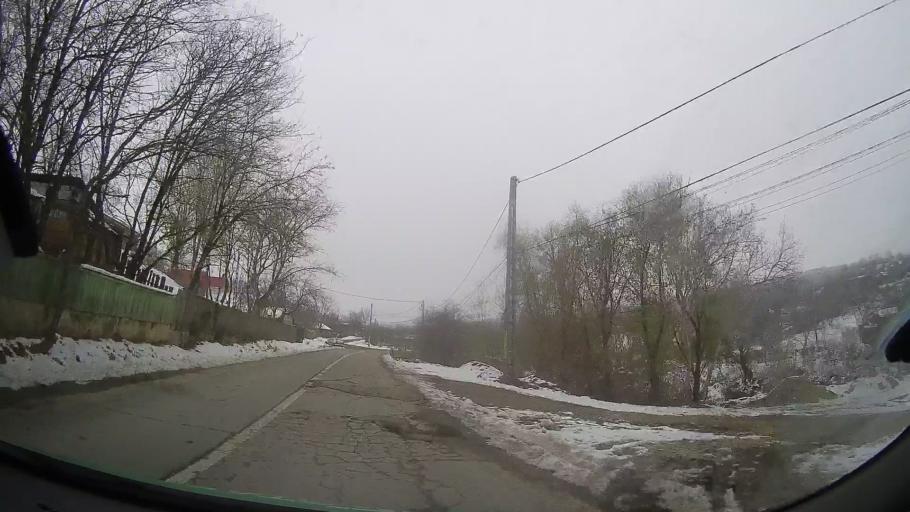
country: RO
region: Vrancea
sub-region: Comuna Boghesti
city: Boghesti
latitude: 46.2027
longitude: 27.4410
